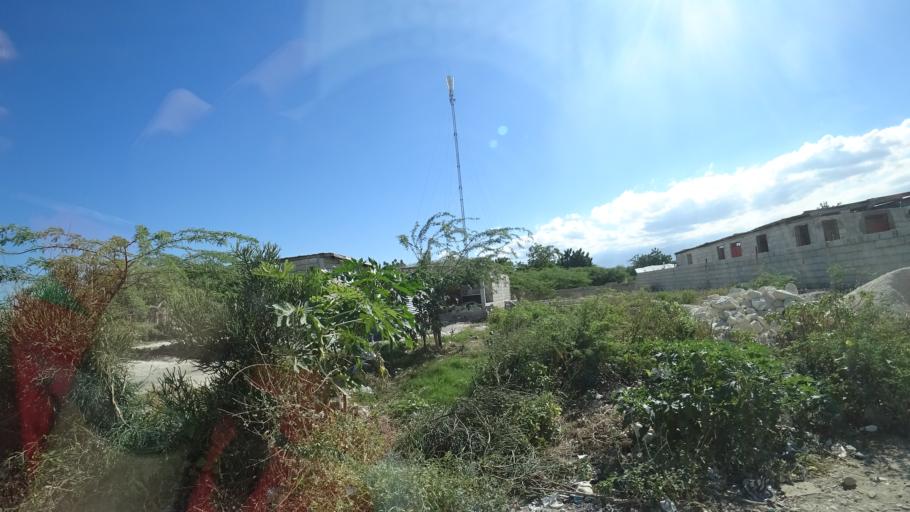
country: HT
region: Ouest
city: Croix des Bouquets
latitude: 18.6512
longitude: -72.2539
